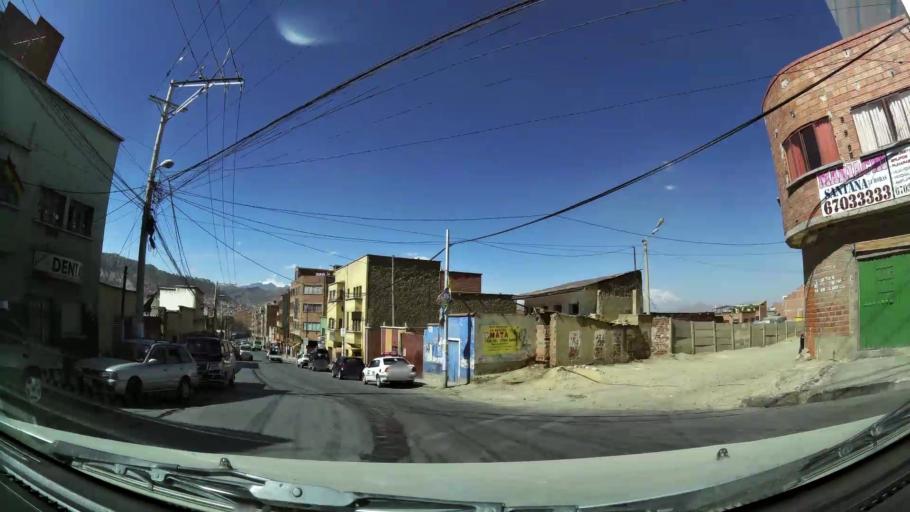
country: BO
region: La Paz
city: La Paz
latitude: -16.4988
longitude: -68.1519
